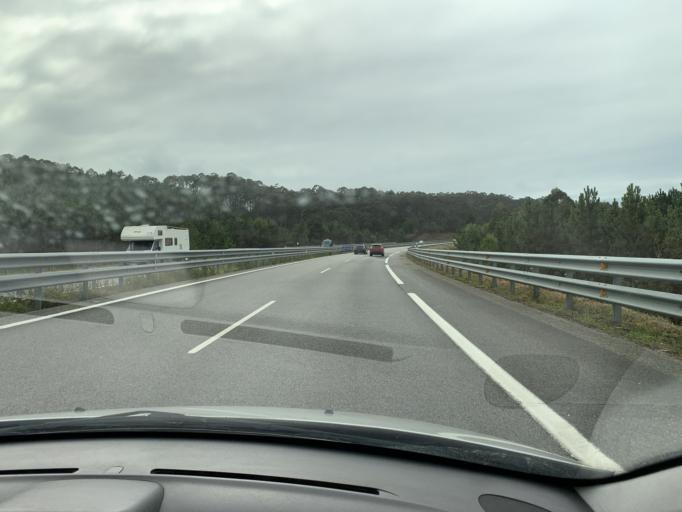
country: ES
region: Asturias
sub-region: Province of Asturias
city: Tineo
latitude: 43.5401
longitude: -6.4218
